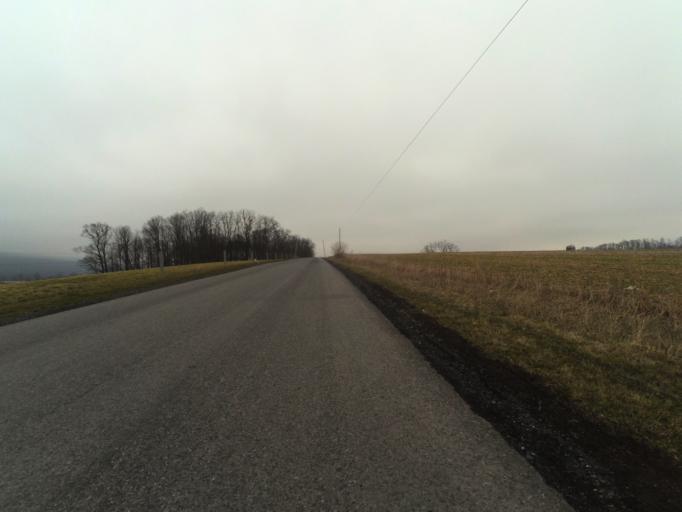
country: US
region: Pennsylvania
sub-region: Centre County
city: Centre Hall
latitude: 40.8583
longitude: -77.6523
